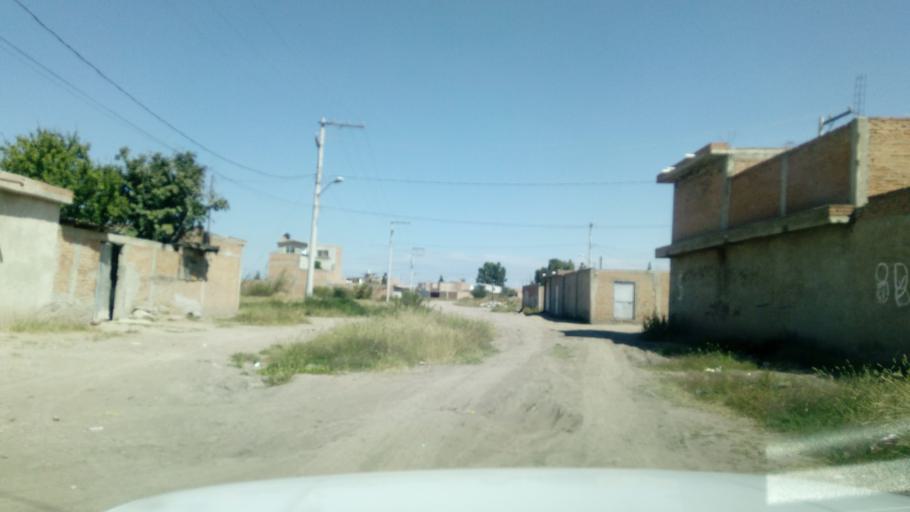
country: MX
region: Durango
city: Victoria de Durango
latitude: 23.9857
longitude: -104.6700
